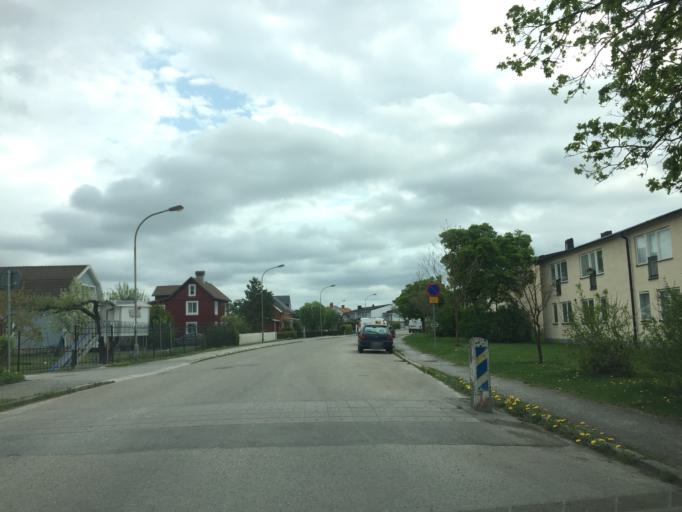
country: SE
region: OErebro
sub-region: Orebro Kommun
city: Orebro
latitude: 59.2842
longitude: 15.1892
